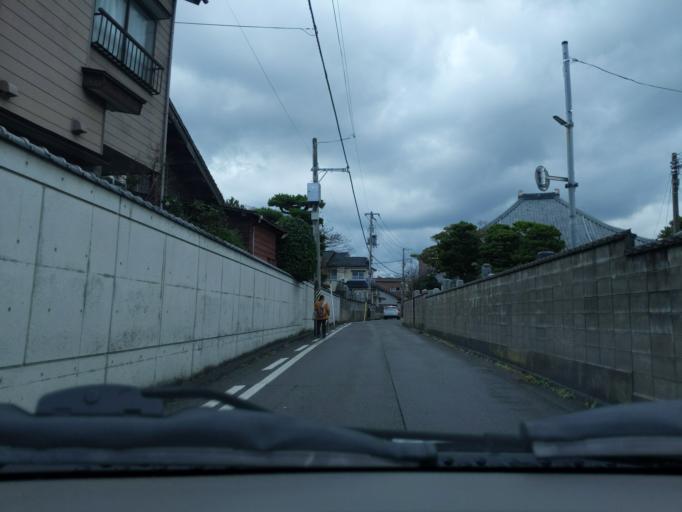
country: JP
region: Niigata
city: Niigata-shi
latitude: 37.9291
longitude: 139.0450
